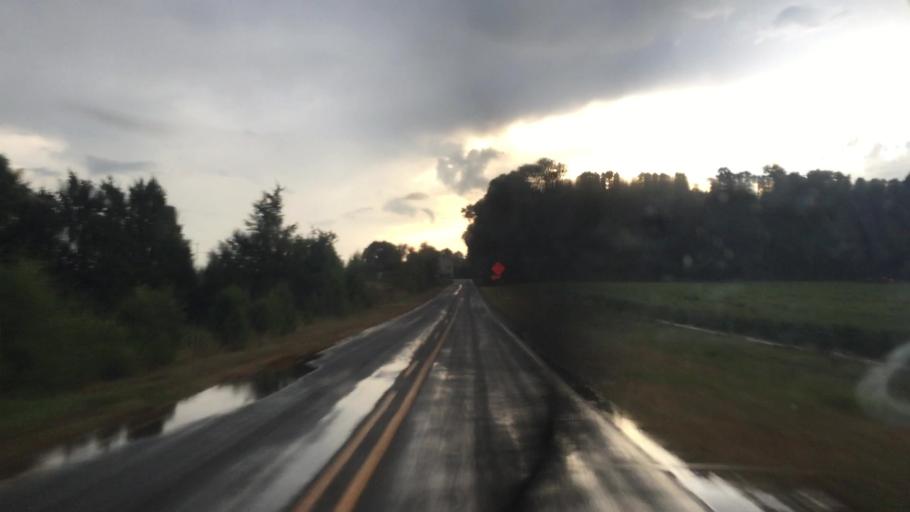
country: US
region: North Carolina
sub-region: Rowan County
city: Enochville
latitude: 35.6385
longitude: -80.6687
